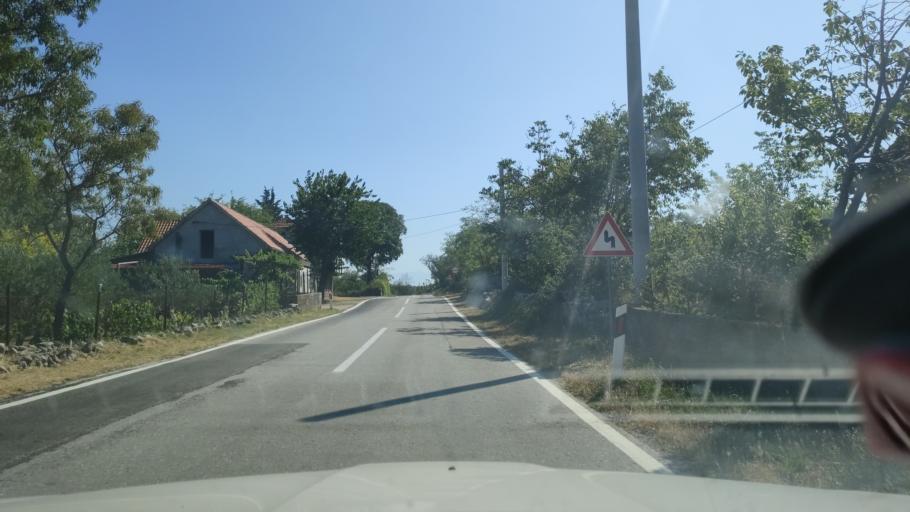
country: HR
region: Sibensko-Kniniska
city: Kistanje
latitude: 43.9569
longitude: 15.8604
